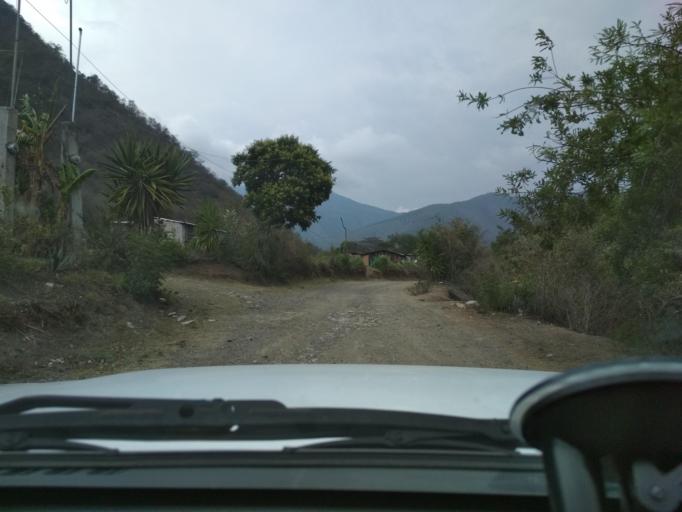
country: MX
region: Veracruz
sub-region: Nogales
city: Taza de Agua Ojo Zarco
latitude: 18.7876
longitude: -97.2109
